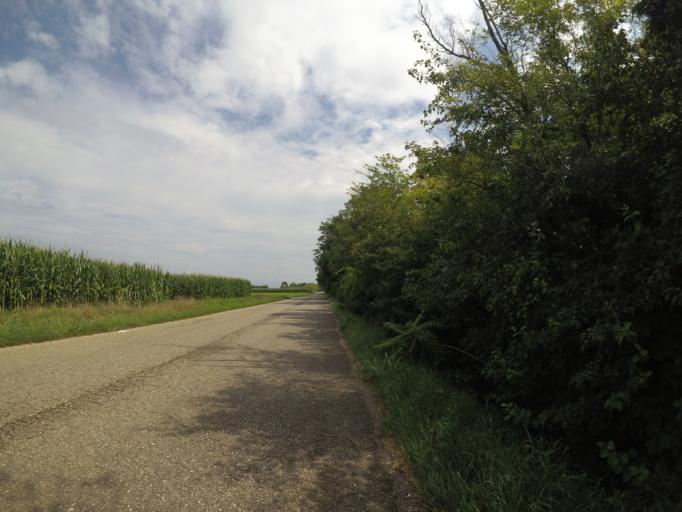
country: IT
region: Friuli Venezia Giulia
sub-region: Provincia di Udine
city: Talmassons
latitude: 45.9467
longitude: 13.1049
